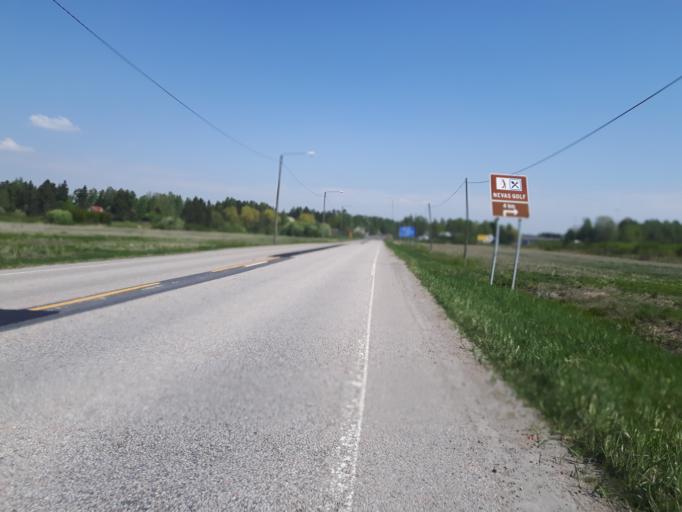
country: FI
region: Uusimaa
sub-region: Helsinki
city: Nickby
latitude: 60.3088
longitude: 25.3820
